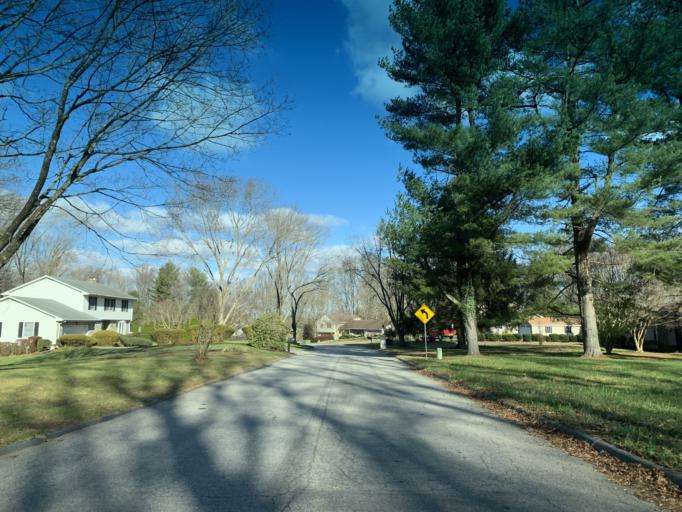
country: US
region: Maryland
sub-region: Harford County
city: South Bel Air
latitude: 39.5786
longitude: -76.2445
